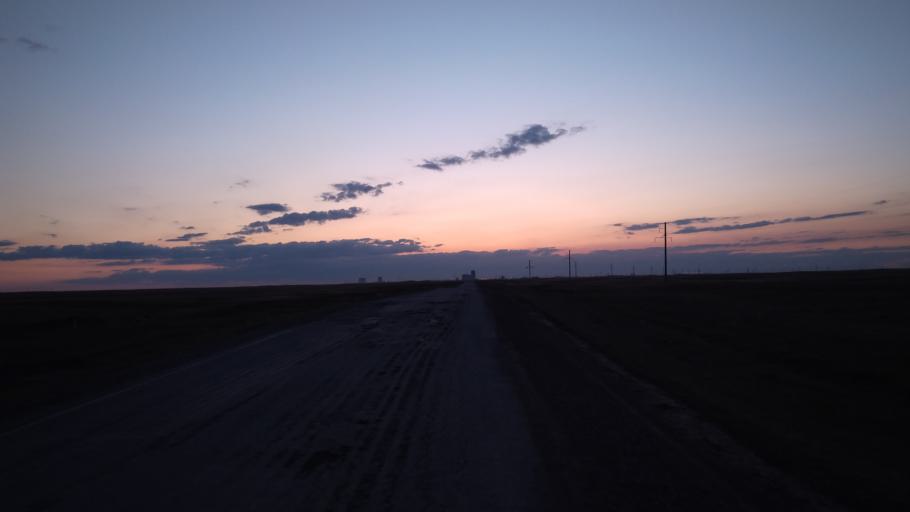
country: RU
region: Chelyabinsk
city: Troitsk
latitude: 54.0908
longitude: 61.6453
